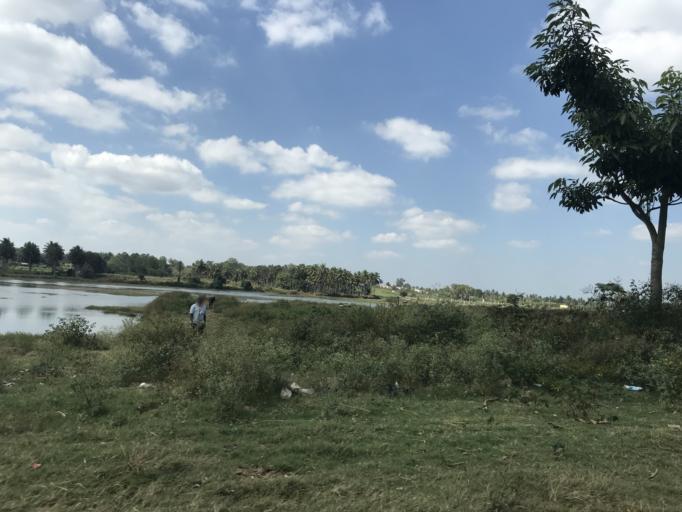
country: IN
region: Karnataka
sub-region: Mysore
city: Hunsur
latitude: 12.2937
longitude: 76.2900
